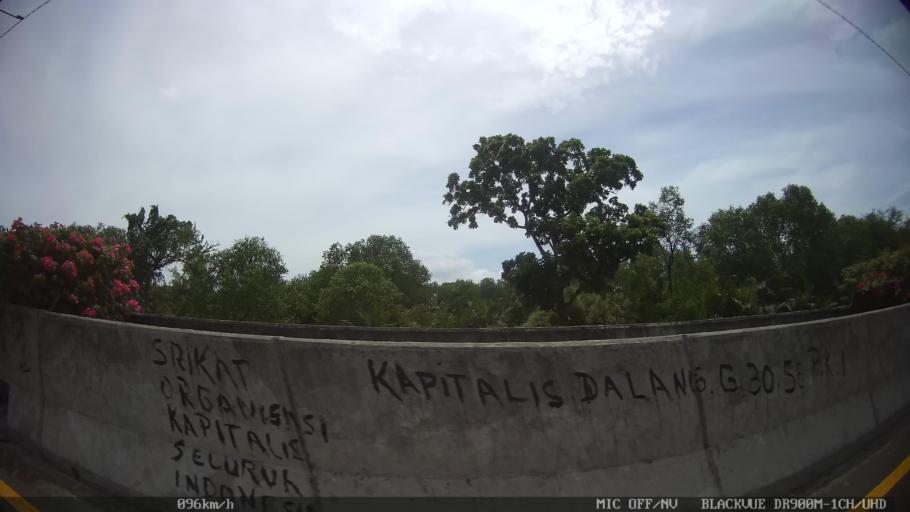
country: ID
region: North Sumatra
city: Labuhan Deli
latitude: 3.7509
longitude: 98.6817
